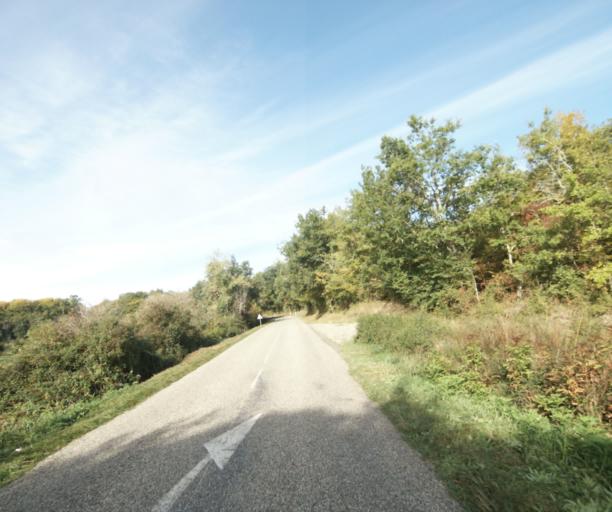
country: FR
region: Midi-Pyrenees
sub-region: Departement du Gers
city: Montreal
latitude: 43.9536
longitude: 0.1346
